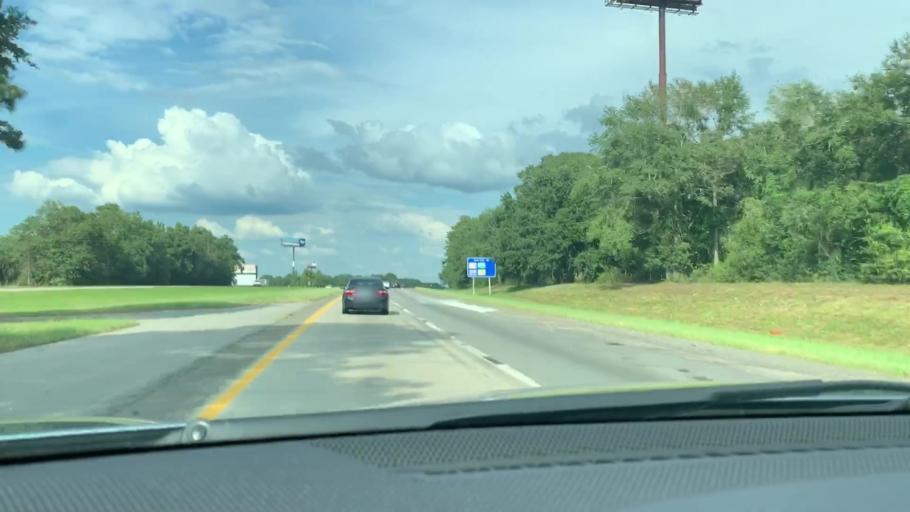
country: US
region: South Carolina
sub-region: Hampton County
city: Yemassee
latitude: 32.6936
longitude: -80.8787
